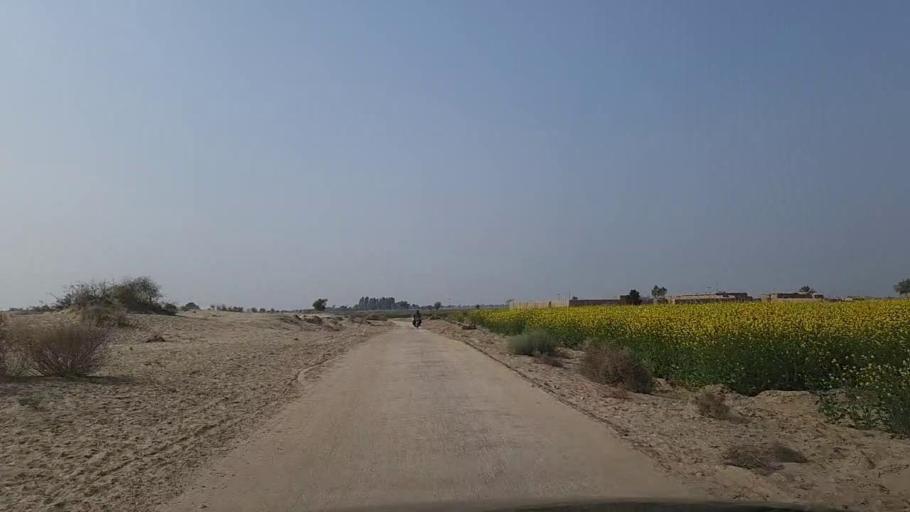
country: PK
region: Sindh
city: Daur
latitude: 26.3861
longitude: 68.4159
